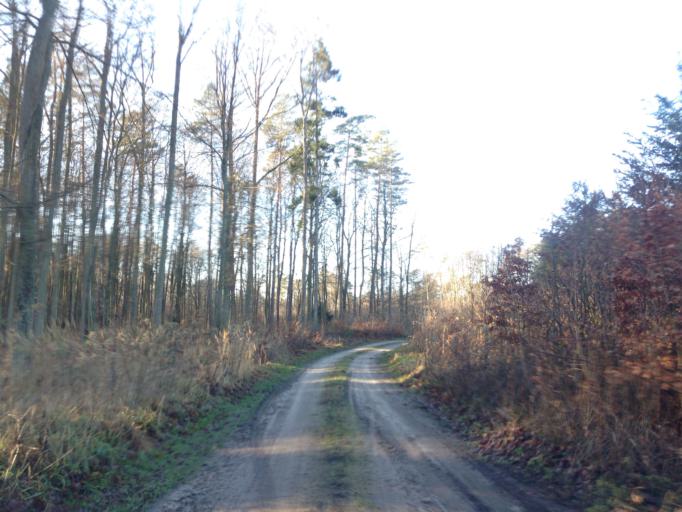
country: PL
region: Pomeranian Voivodeship
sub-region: Powiat kwidzynski
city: Gardeja
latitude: 53.6334
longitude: 19.0235
